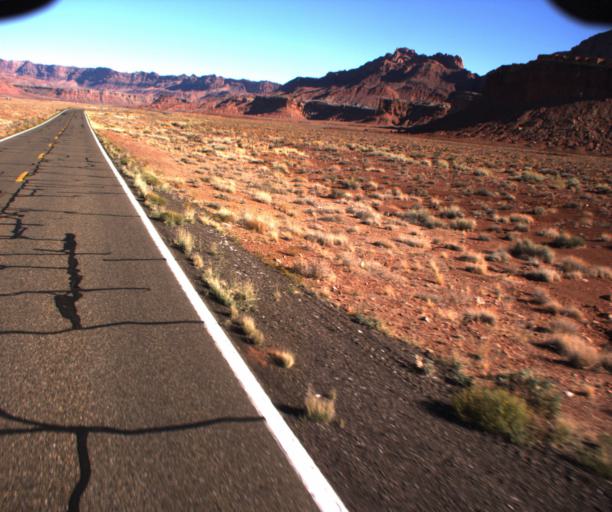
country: US
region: Arizona
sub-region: Coconino County
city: LeChee
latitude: 36.7947
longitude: -111.6122
